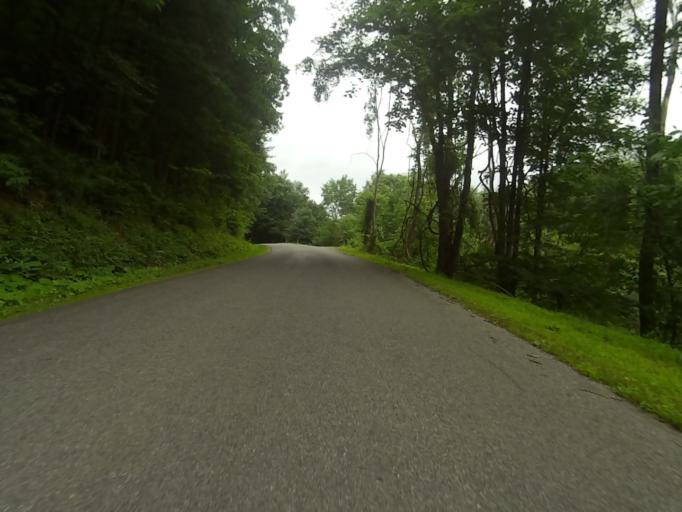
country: US
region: Pennsylvania
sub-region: Centre County
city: Stormstown
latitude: 40.6985
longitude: -78.0950
